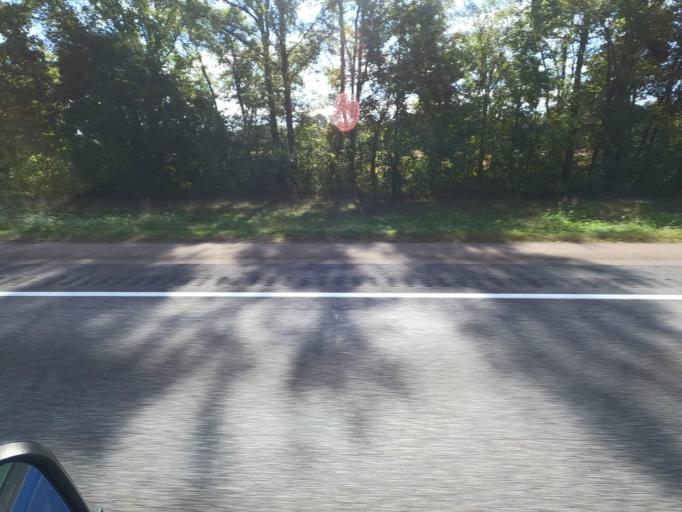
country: US
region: Tennessee
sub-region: Haywood County
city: Brownsville
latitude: 35.5481
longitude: -89.2121
